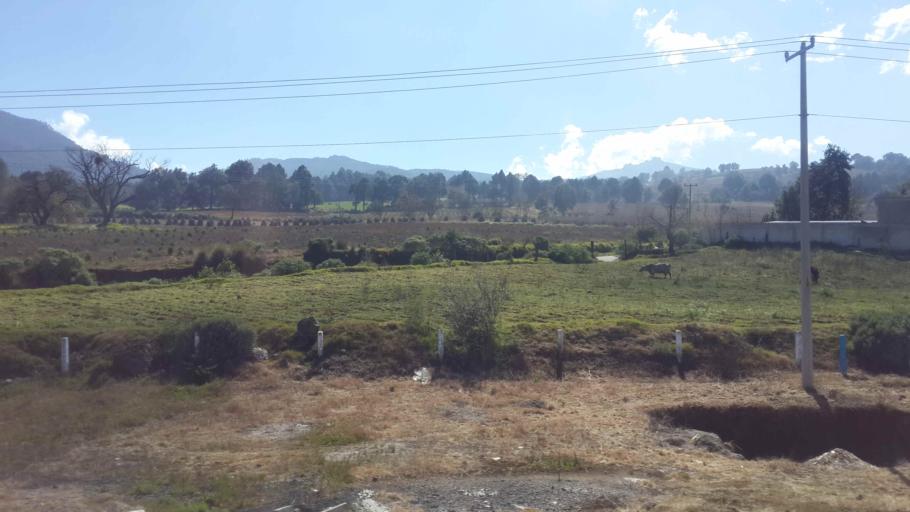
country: MX
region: Veracruz
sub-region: Las Vigas de Ramirez
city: Barrio de San Miguel
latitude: 19.6305
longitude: -97.1263
